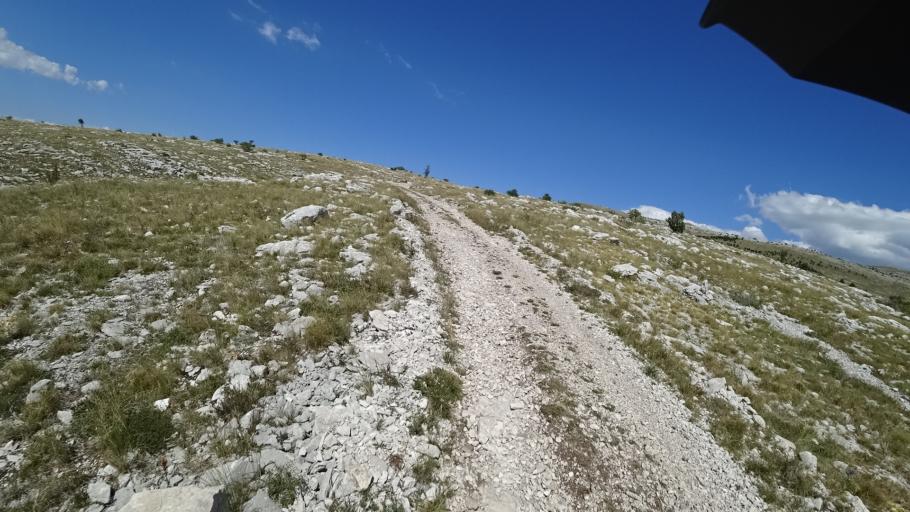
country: HR
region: Splitsko-Dalmatinska
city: Hrvace
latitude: 43.8621
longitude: 16.6398
